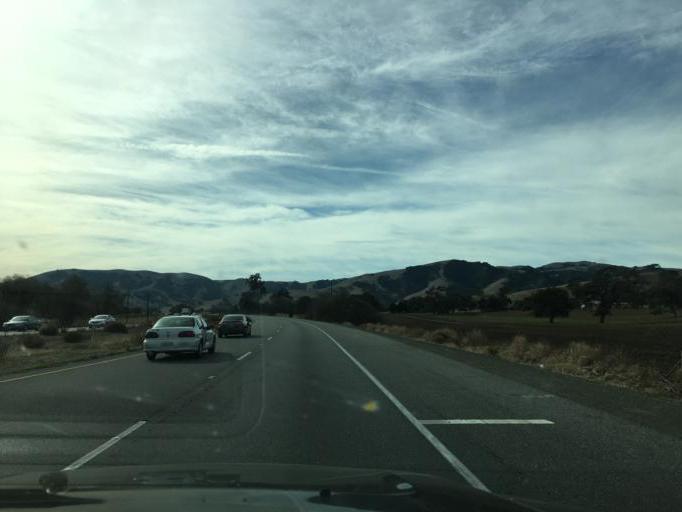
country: US
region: California
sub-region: San Benito County
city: Hollister
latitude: 37.0065
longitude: -121.3660
